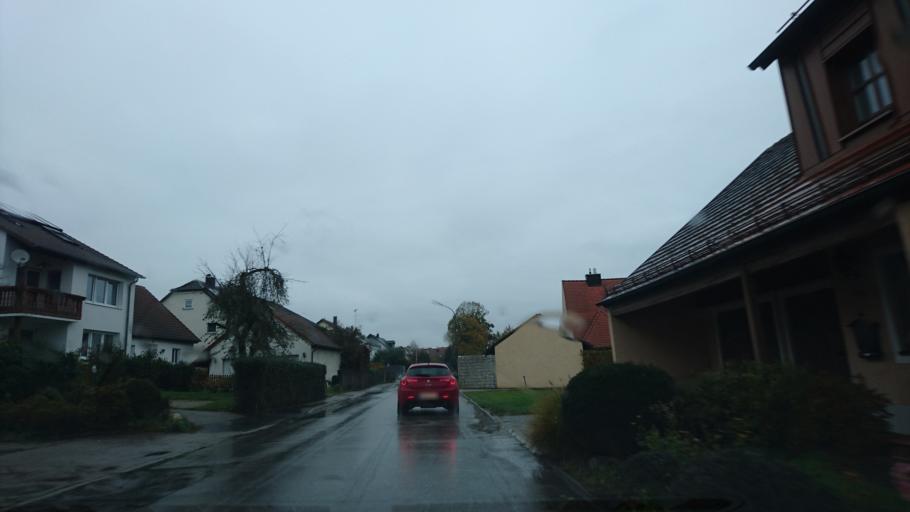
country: DE
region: Bavaria
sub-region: Upper Bavaria
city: Petershausen
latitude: 48.4117
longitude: 11.4723
